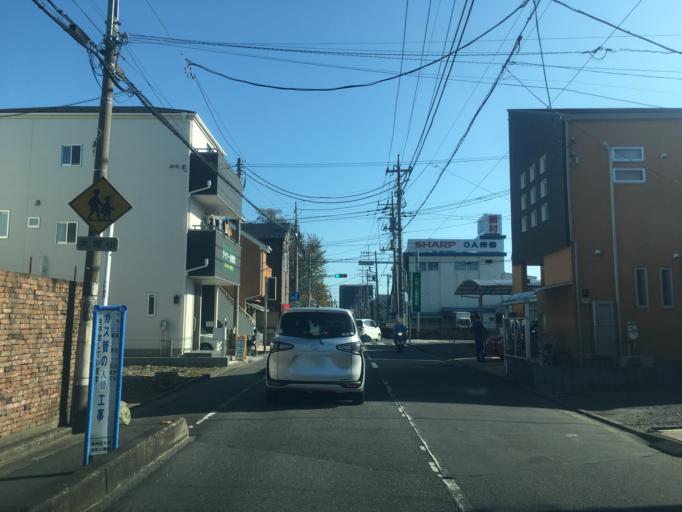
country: JP
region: Saitama
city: Kawagoe
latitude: 35.9000
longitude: 139.4698
